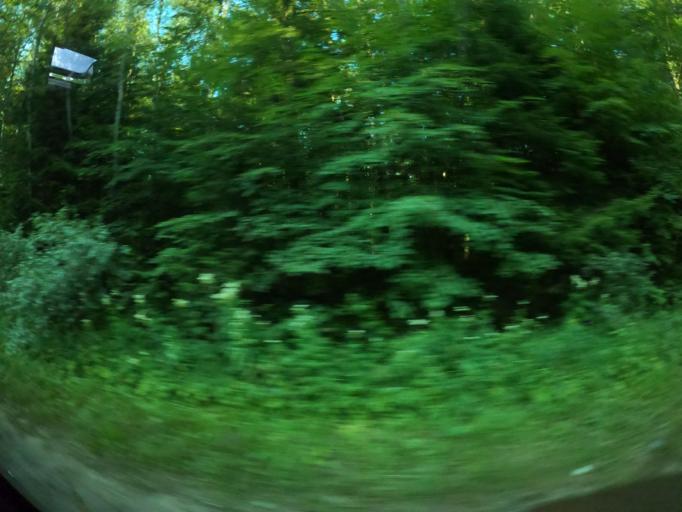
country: RU
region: Moskovskaya
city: Obolensk
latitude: 54.9859
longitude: 37.2104
